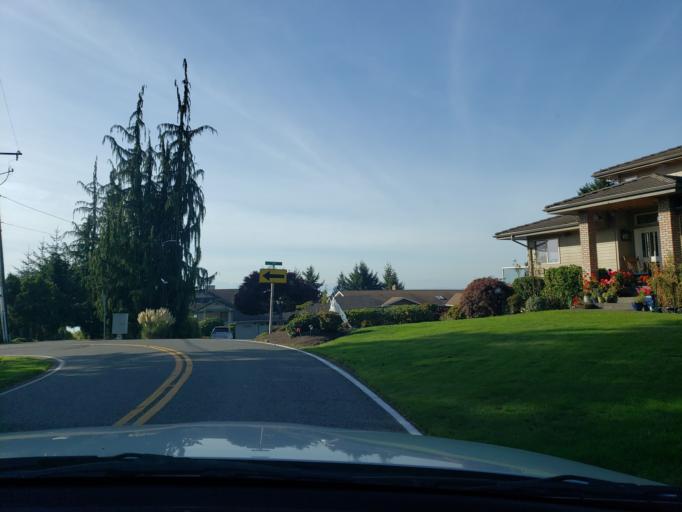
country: US
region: Washington
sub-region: Snohomish County
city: Meadowdale
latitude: 47.8629
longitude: -122.3302
